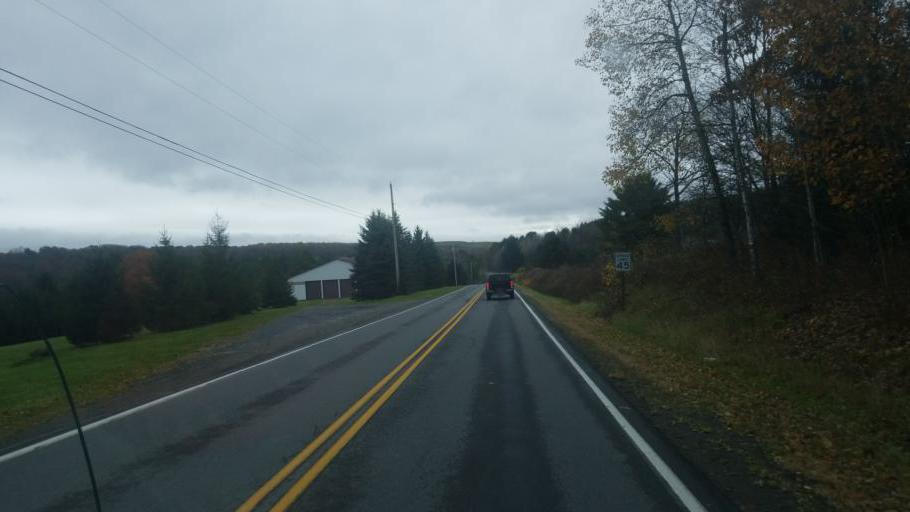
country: US
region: Pennsylvania
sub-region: Elk County
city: Ridgway
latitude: 41.3077
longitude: -78.6606
